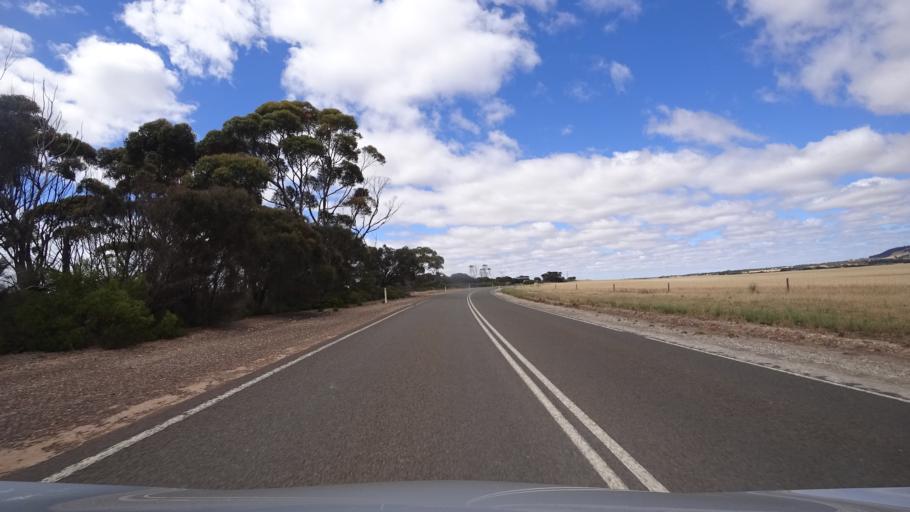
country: AU
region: South Australia
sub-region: Kangaroo Island
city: Kingscote
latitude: -35.6309
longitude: 137.5582
